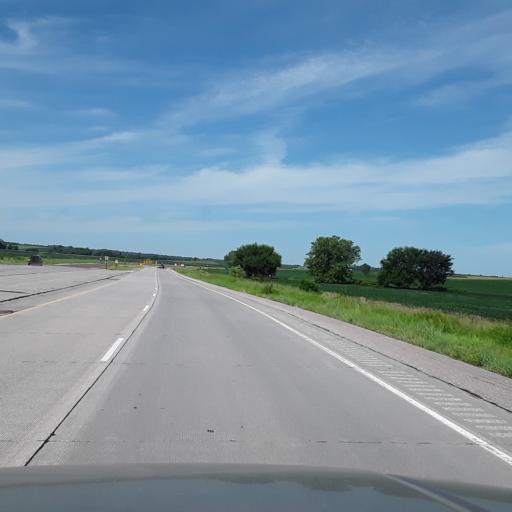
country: US
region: Nebraska
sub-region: Lancaster County
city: Lincoln
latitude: 40.8879
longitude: -96.8028
